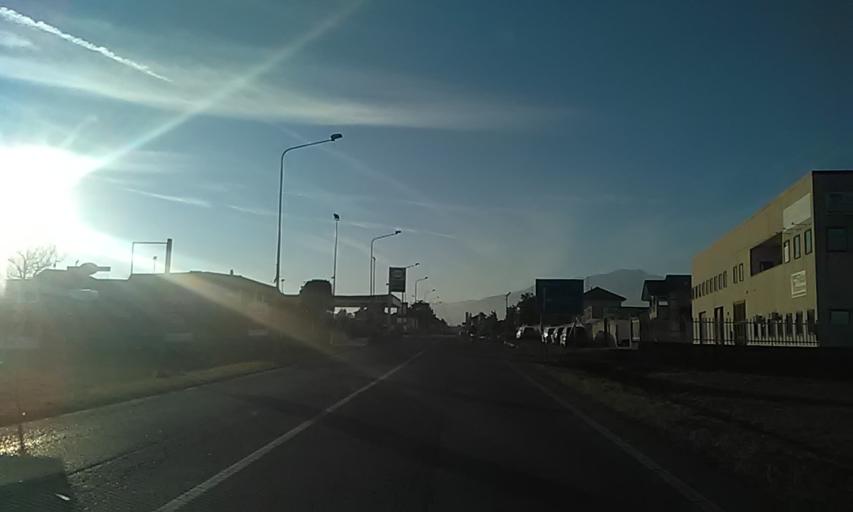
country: IT
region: Piedmont
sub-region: Provincia di Biella
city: Valdengo
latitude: 45.5632
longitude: 8.1357
